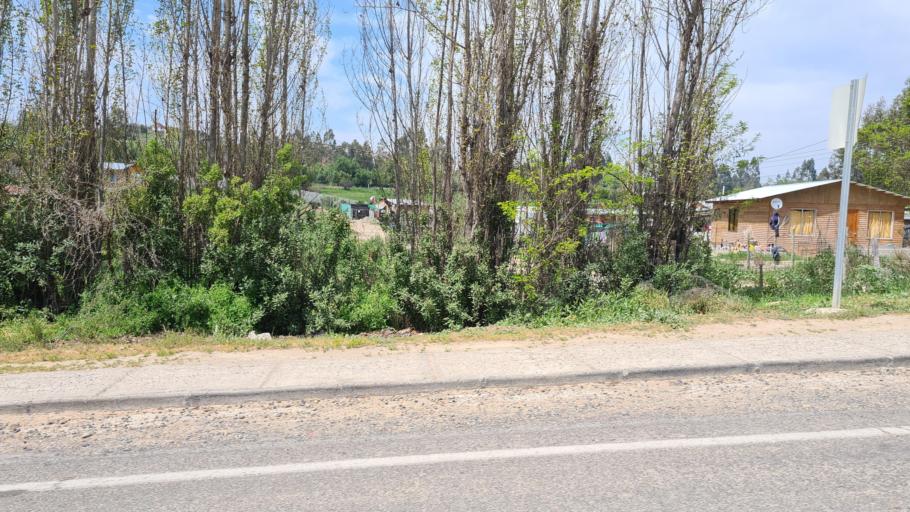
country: CL
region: O'Higgins
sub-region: Provincia de Cachapoal
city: San Vicente
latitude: -34.1595
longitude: -71.4265
